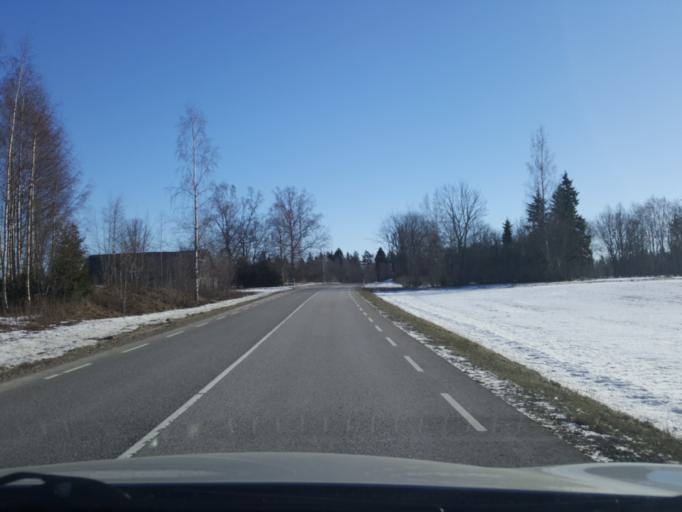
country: EE
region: Viljandimaa
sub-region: Vohma linn
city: Vohma
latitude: 58.5249
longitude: 25.6130
